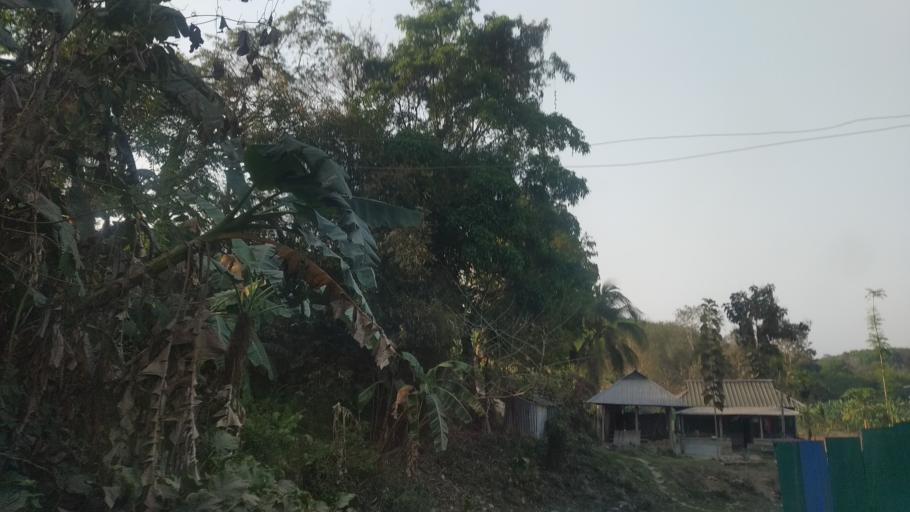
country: IN
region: Tripura
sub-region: West Tripura
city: Sonamura
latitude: 23.4407
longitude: 91.3627
